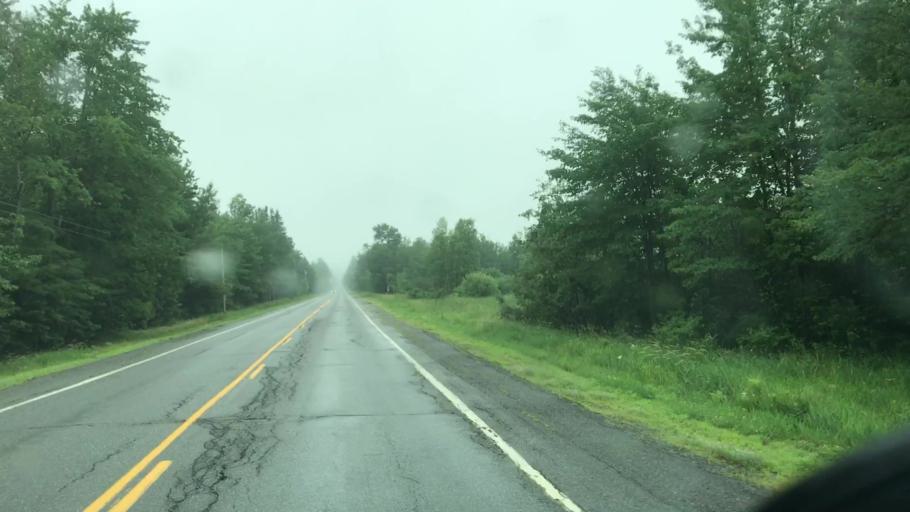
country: US
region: Maine
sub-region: Penobscot County
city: Howland
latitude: 45.2502
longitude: -68.6383
